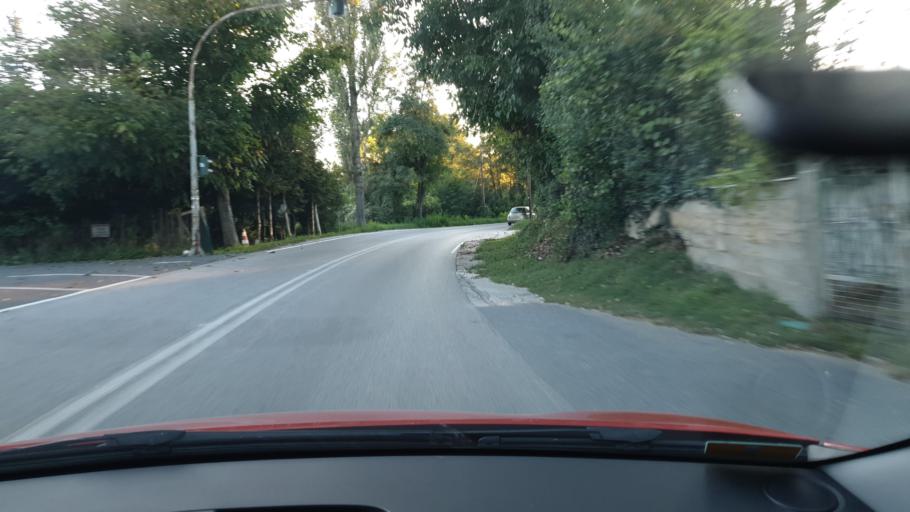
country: GR
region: Central Macedonia
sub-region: Nomos Chalkidikis
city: Galatista
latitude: 40.4649
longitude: 23.3752
